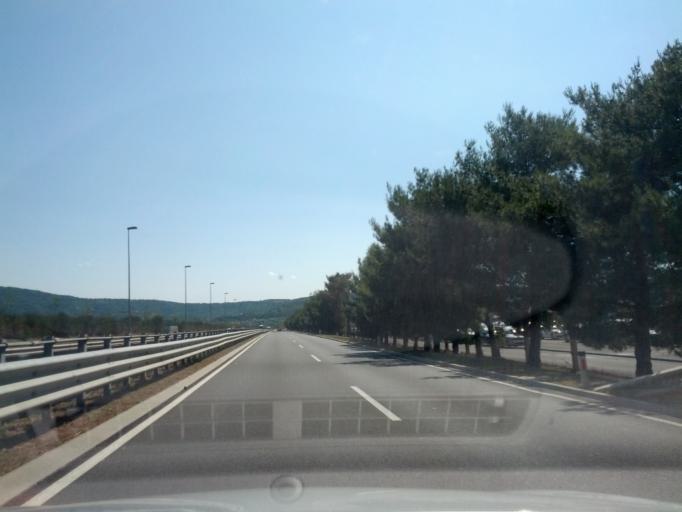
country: SI
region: Koper-Capodistria
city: Koper
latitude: 45.5508
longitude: 13.7510
